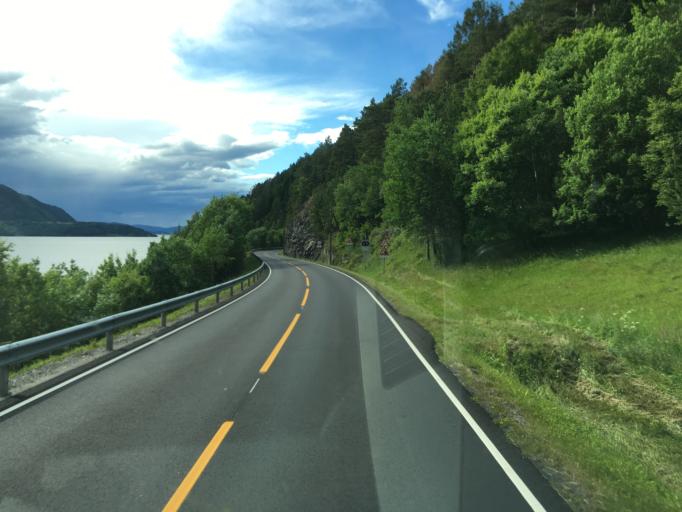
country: NO
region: More og Romsdal
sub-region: Tingvoll
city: Tingvoll
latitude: 62.9555
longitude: 8.1167
